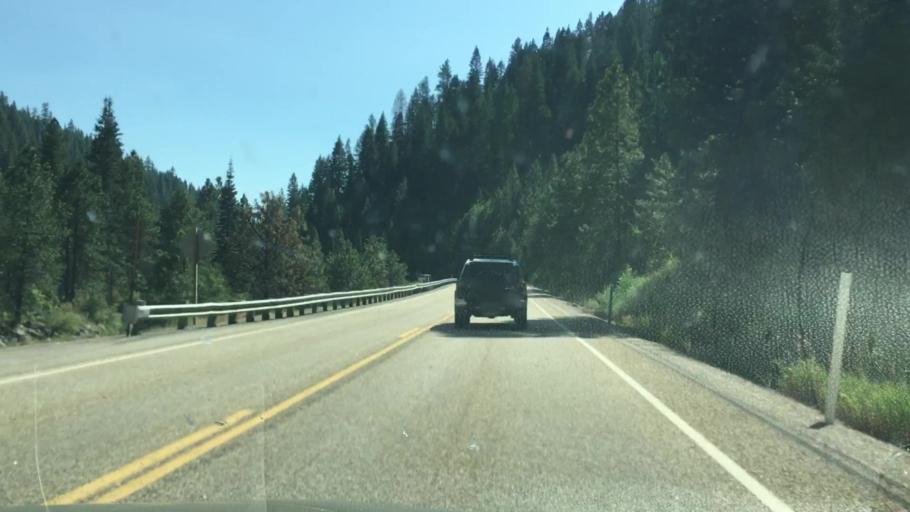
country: US
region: Idaho
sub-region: Valley County
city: Cascade
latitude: 44.2072
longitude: -116.1087
